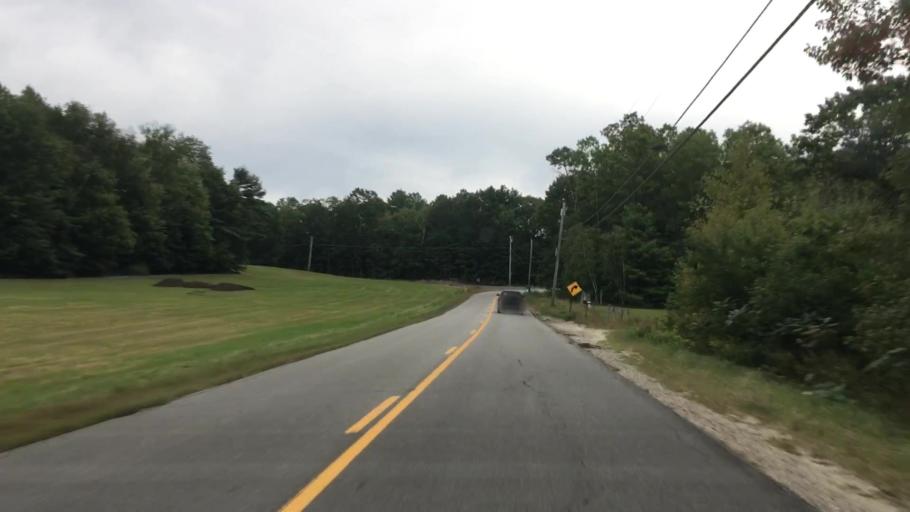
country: US
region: Maine
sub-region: Cumberland County
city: Freeport
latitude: 43.8896
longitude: -70.1765
